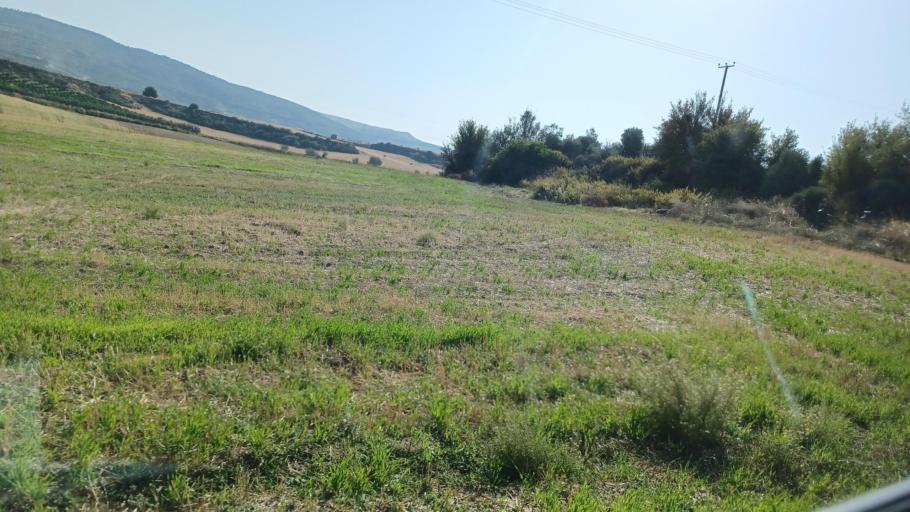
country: CY
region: Pafos
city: Polis
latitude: 35.0150
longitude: 32.4416
